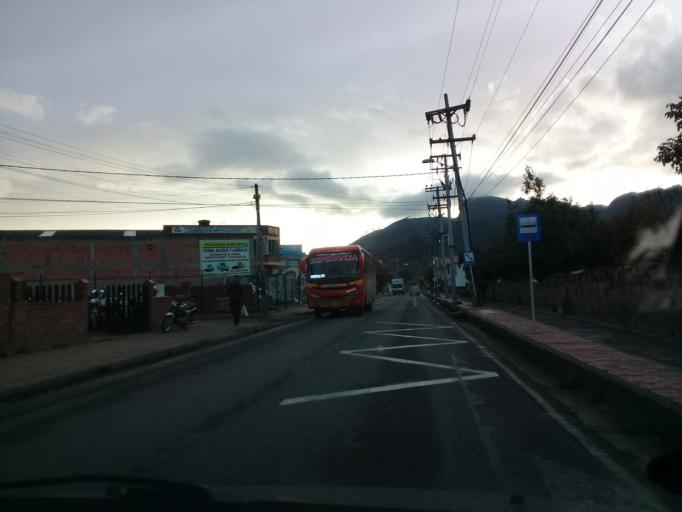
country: CO
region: Cundinamarca
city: Tabio
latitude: 4.9199
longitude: -74.0904
